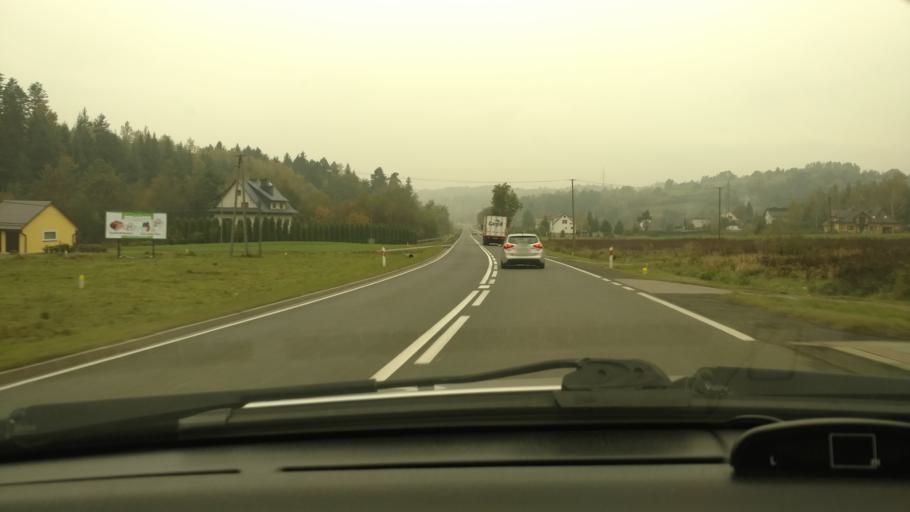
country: PL
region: Lesser Poland Voivodeship
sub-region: Powiat nowosadecki
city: Kamionka Wielka
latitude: 49.6191
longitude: 20.7947
